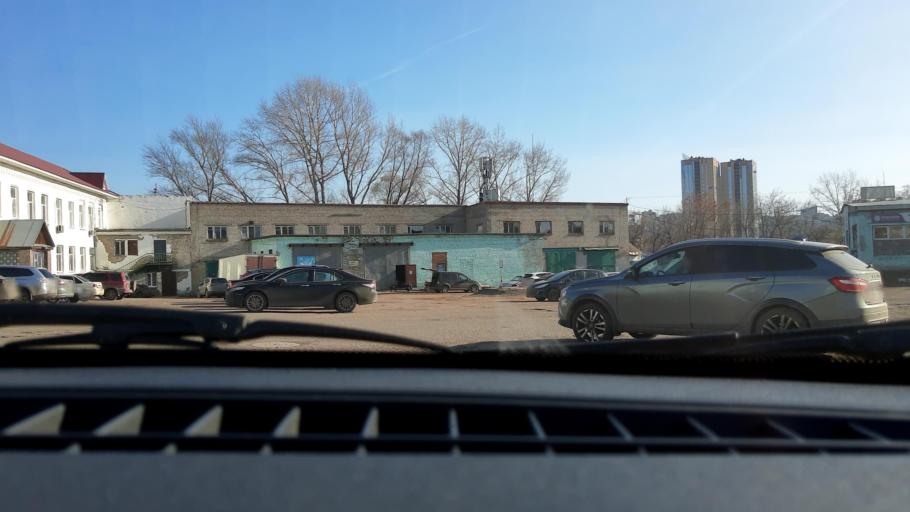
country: RU
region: Bashkortostan
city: Ufa
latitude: 54.7287
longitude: 55.9902
